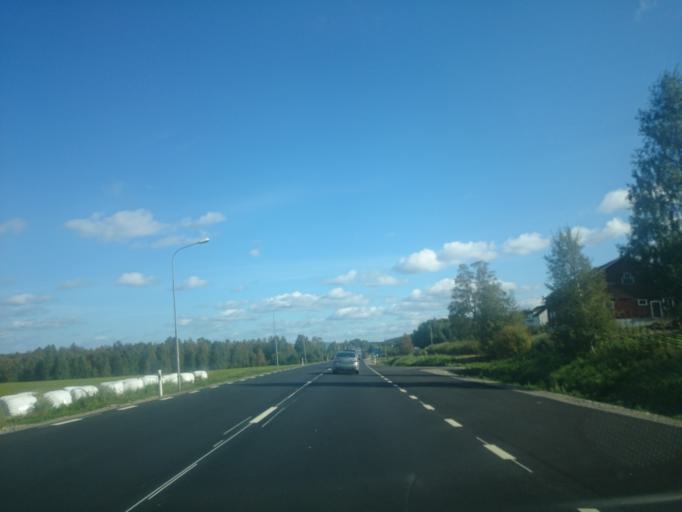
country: SE
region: Gaevleborg
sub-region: Ljusdals Kommun
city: Ljusdal
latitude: 61.8235
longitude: 16.0491
